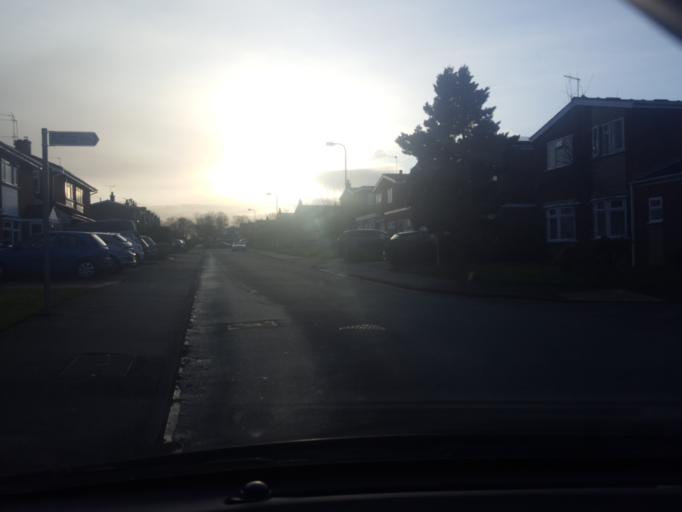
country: GB
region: England
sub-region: Staffordshire
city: Codsall
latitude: 52.6319
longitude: -2.1957
